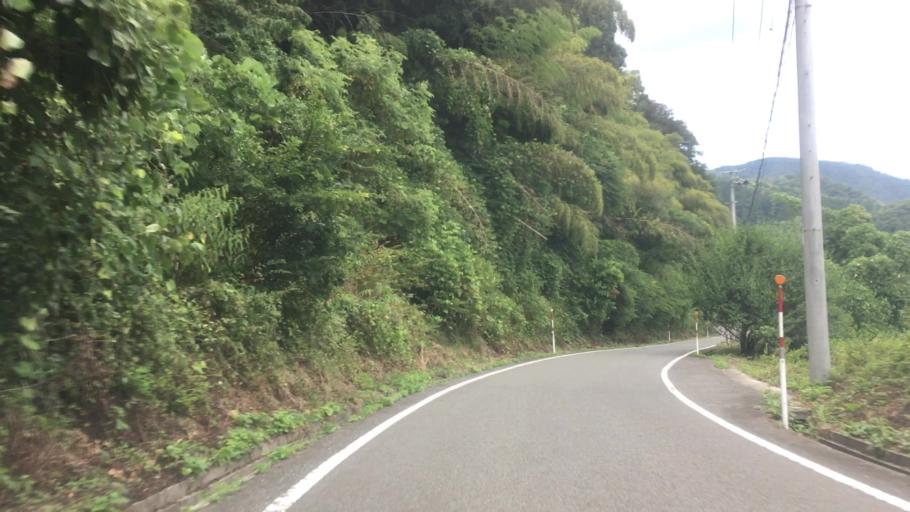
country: JP
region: Hyogo
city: Toyooka
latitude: 35.5876
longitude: 134.7982
